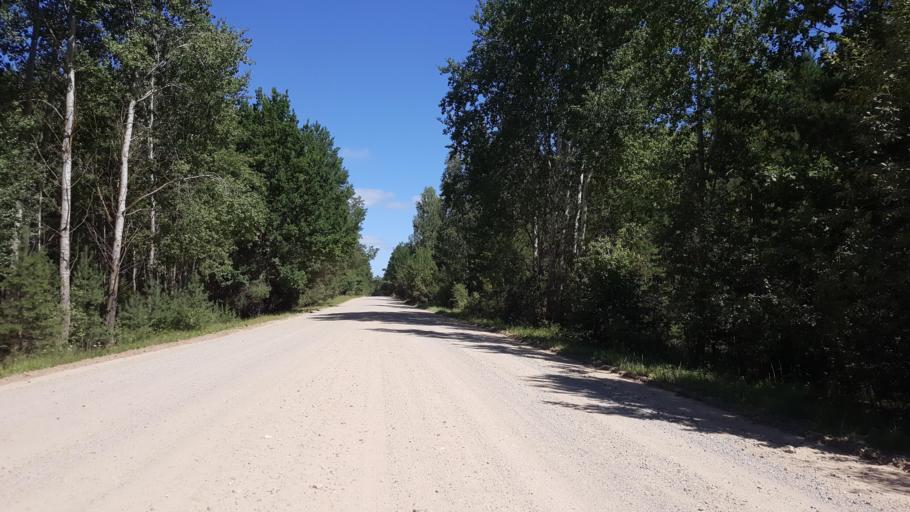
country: BY
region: Brest
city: Kobryn
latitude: 52.3603
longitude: 24.2780
